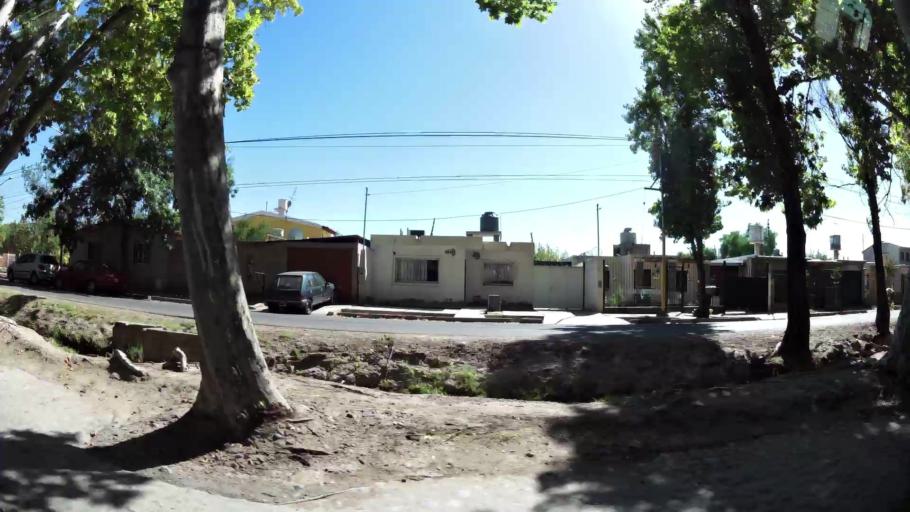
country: AR
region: Mendoza
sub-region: Departamento de Maipu
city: Maipu
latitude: -32.9478
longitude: -68.7980
